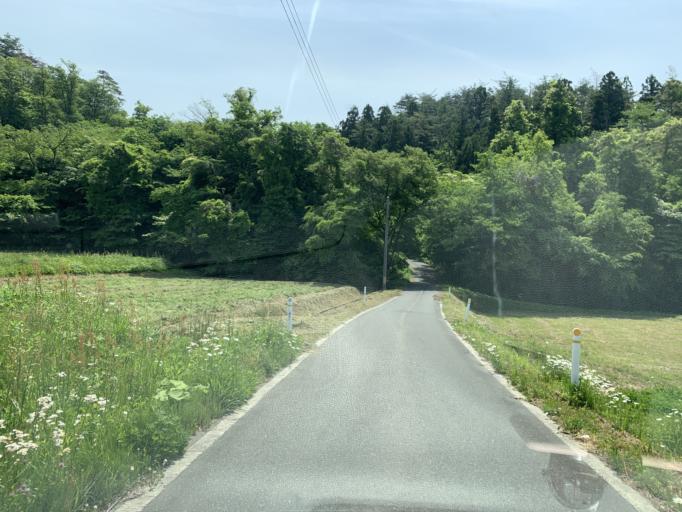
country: JP
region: Iwate
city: Ichinoseki
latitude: 38.9717
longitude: 141.2209
